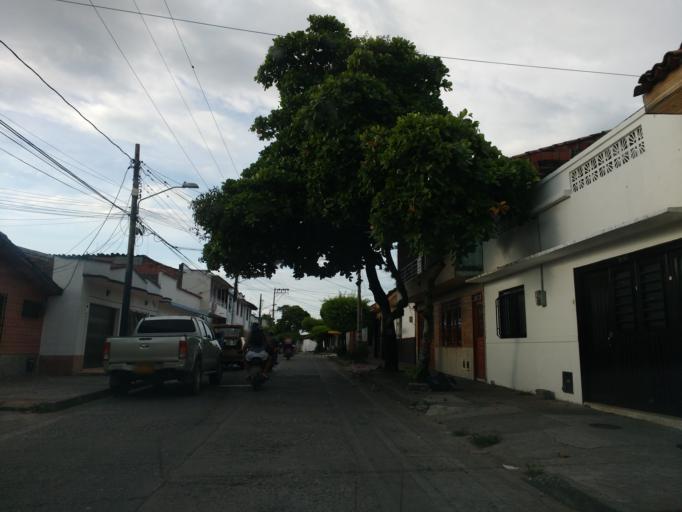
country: CO
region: Valle del Cauca
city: Cartago
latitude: 4.7468
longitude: -75.9200
